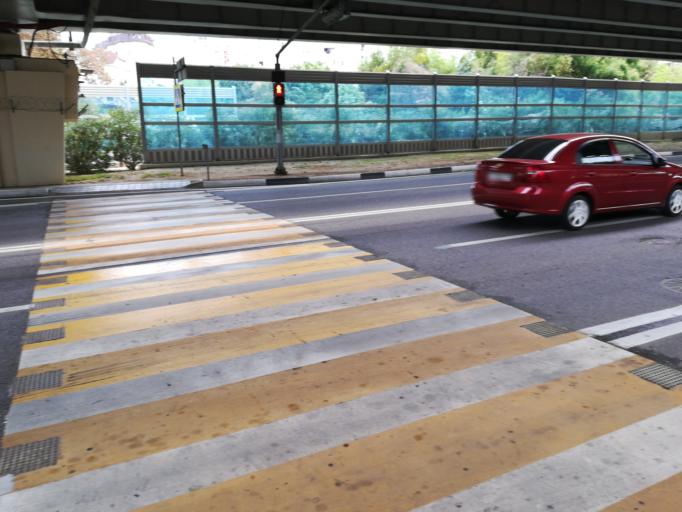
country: RU
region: Krasnodarskiy
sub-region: Sochi City
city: Sochi
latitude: 43.5918
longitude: 39.7302
